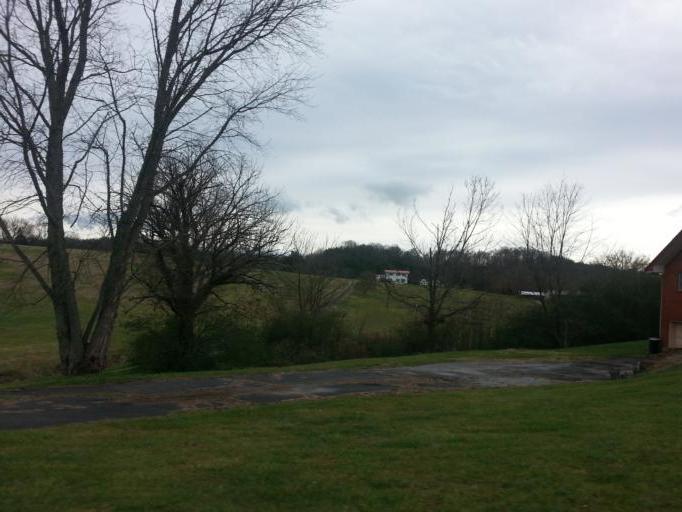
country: US
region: Tennessee
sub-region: Greene County
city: Greeneville
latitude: 36.1235
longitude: -82.8985
